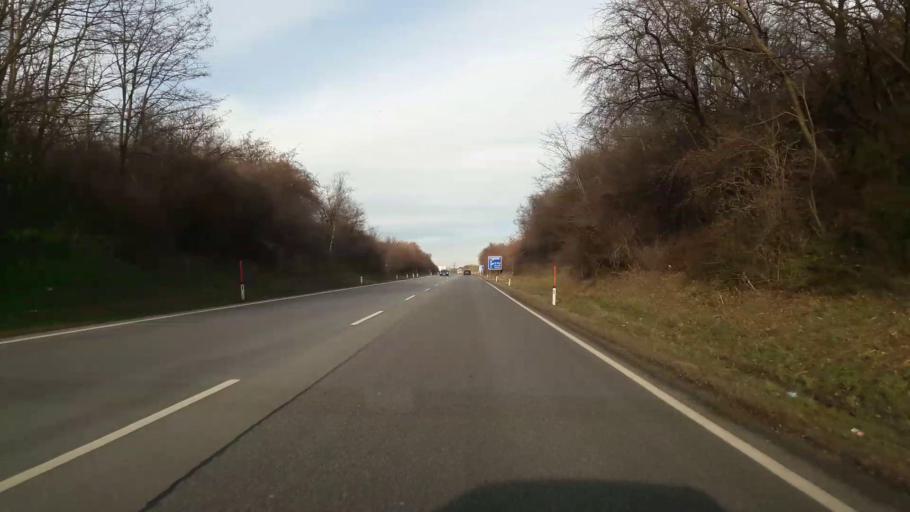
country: AT
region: Lower Austria
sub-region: Politischer Bezirk Mistelbach
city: Gaweinstal
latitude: 48.4898
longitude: 16.5961
